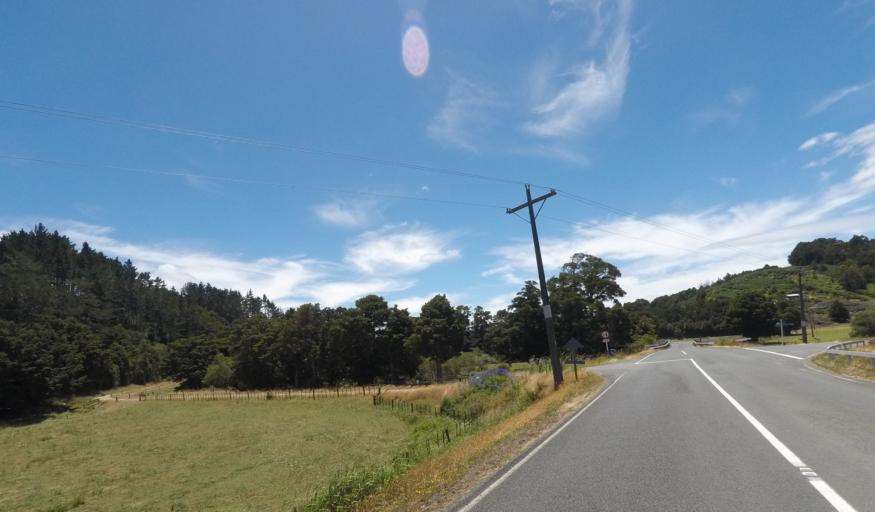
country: NZ
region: Northland
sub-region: Whangarei
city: Whangarei
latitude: -35.5427
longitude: 174.3082
